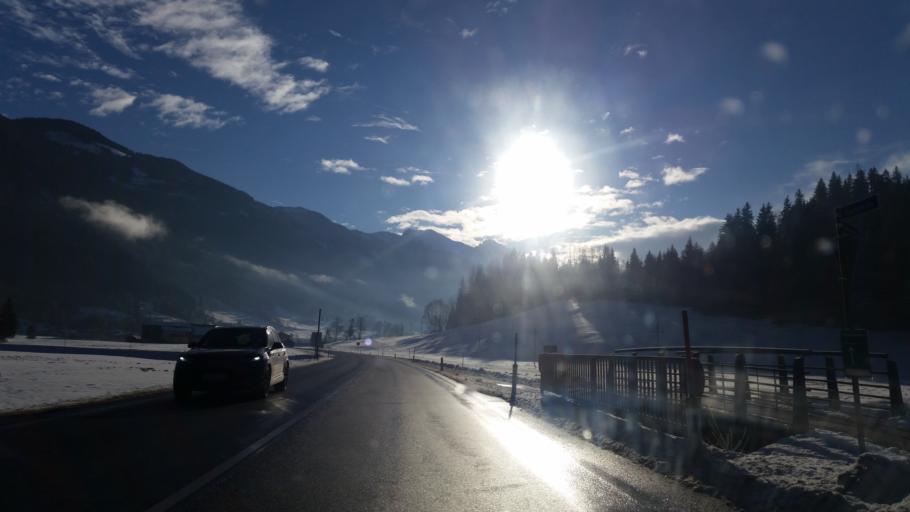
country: AT
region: Salzburg
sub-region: Politischer Bezirk Sankt Johann im Pongau
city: Radstadt
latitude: 47.3682
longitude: 13.4825
